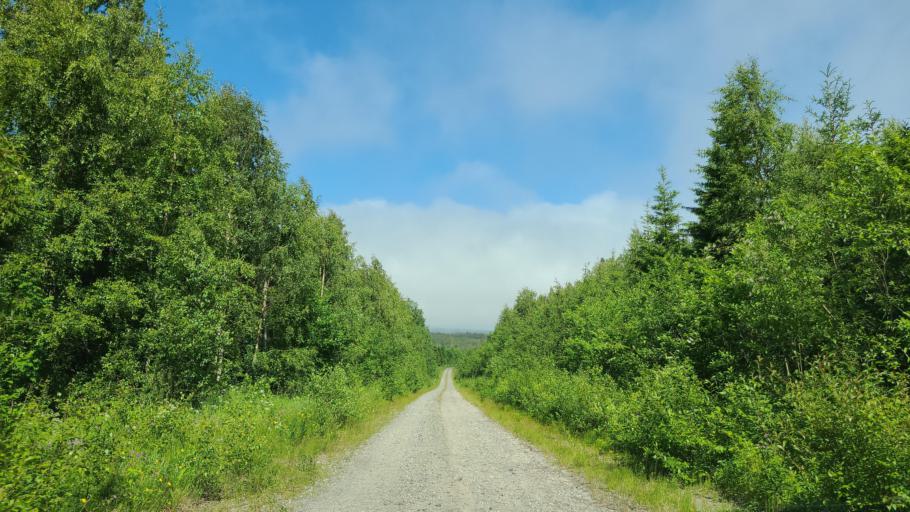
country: SE
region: Vaesternorrland
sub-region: OErnskoeldsviks Kommun
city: Husum
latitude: 63.4509
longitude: 19.2378
